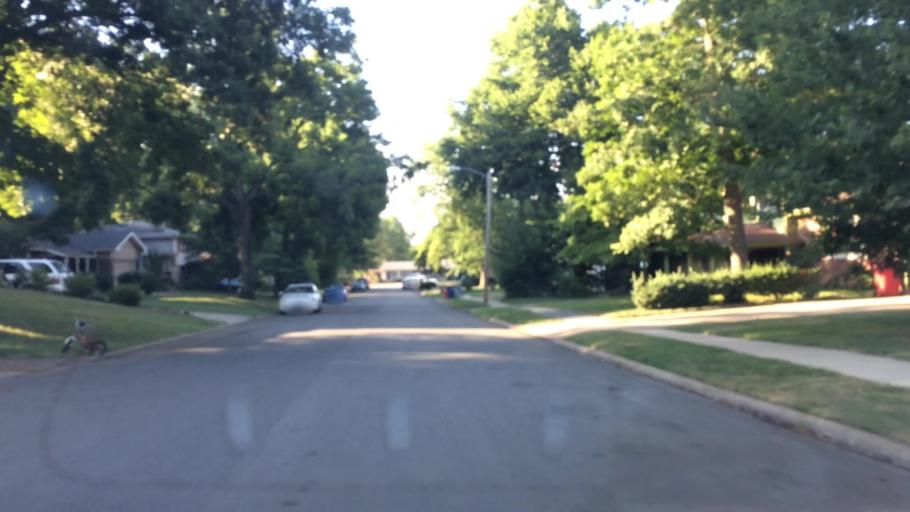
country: US
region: Missouri
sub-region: Greene County
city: Springfield
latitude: 37.2019
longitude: -93.2566
